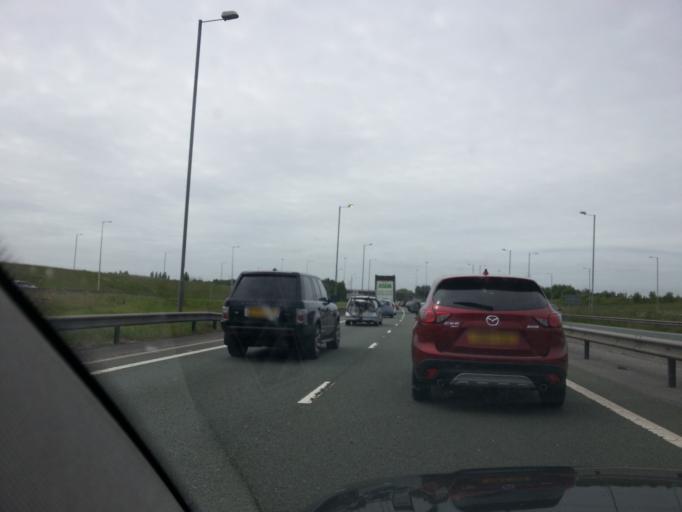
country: GB
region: England
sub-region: Cheshire West and Chester
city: Shotwick
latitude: 53.2330
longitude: -2.9911
